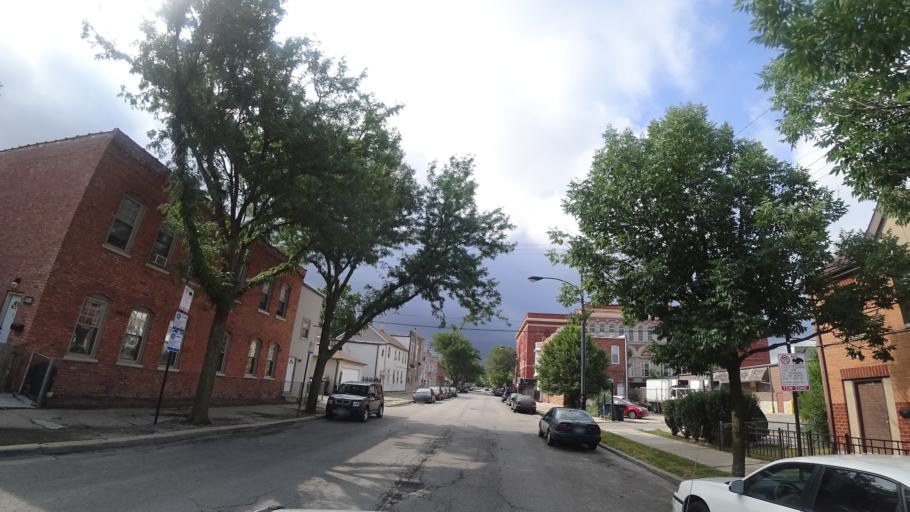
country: US
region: Illinois
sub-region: Cook County
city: Chicago
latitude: 41.8537
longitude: -87.6833
